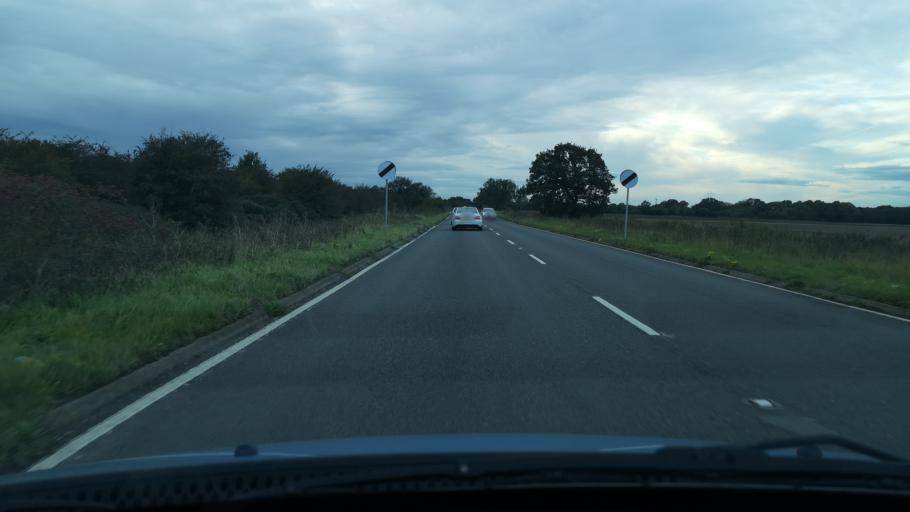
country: GB
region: England
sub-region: North Lincolnshire
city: Belton
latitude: 53.5810
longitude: -0.7967
